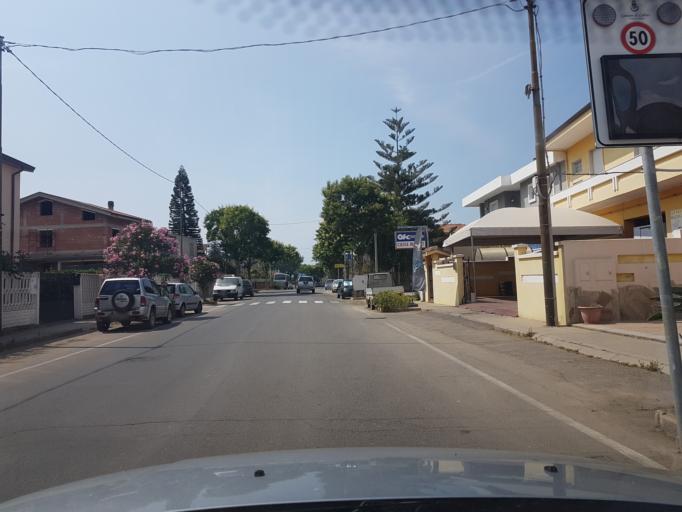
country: IT
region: Sardinia
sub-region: Provincia di Oristano
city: Cabras
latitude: 39.9231
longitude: 8.5414
